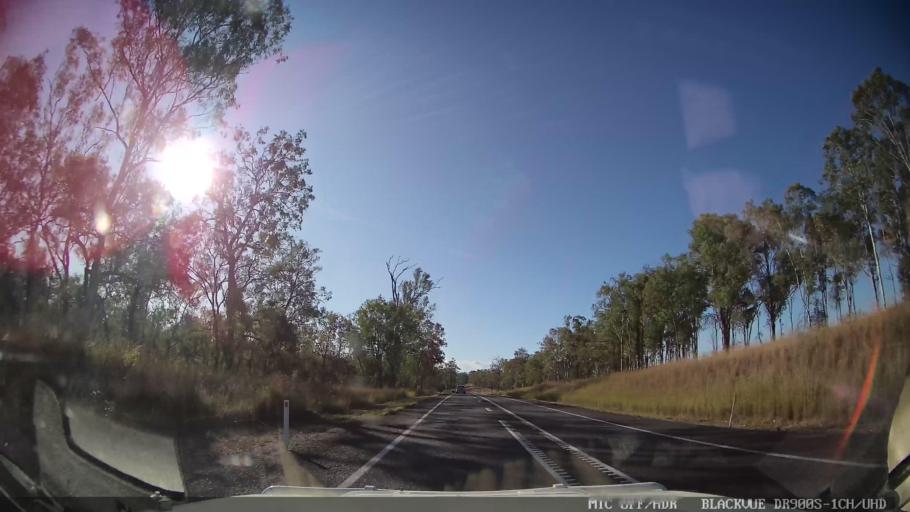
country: AU
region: Queensland
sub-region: Bundaberg
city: Sharon
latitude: -24.8365
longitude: 151.7101
